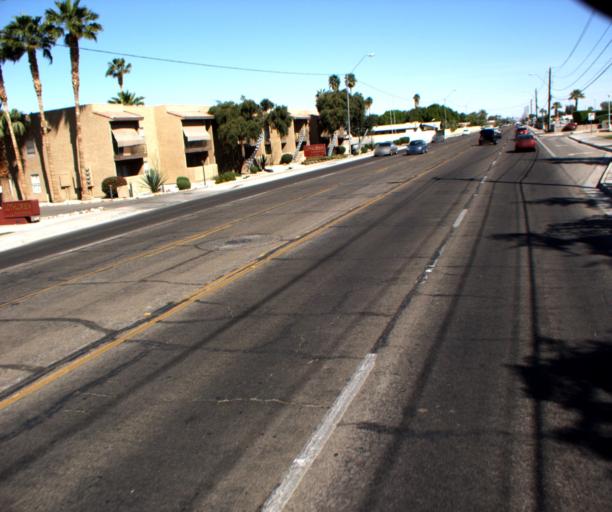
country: US
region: Arizona
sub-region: Yuma County
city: Yuma
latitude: 32.6865
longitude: -114.6503
